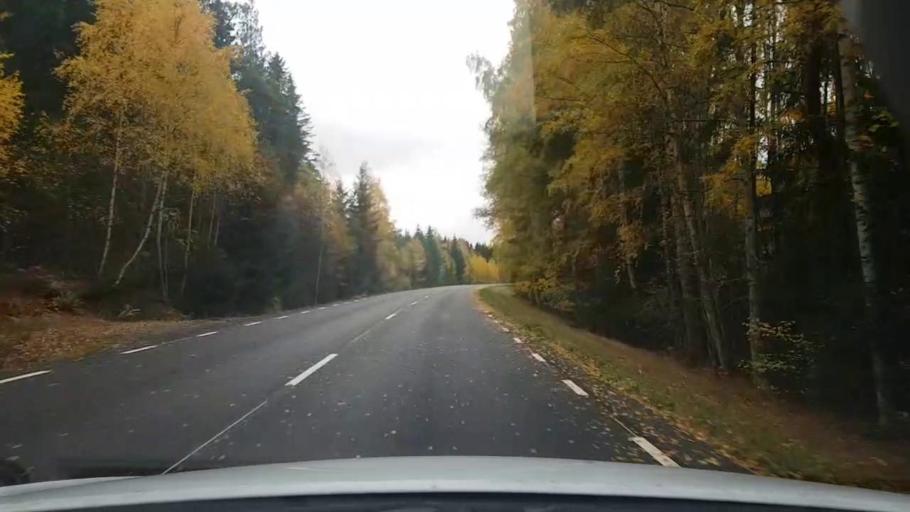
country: SE
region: OErebro
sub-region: Laxa Kommun
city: Laxa
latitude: 58.7736
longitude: 14.5360
